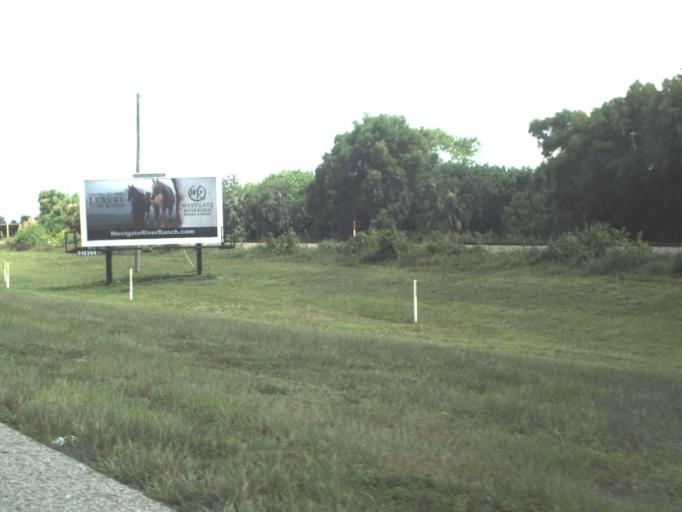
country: US
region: Florida
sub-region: Palm Beach County
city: Mangonia Park
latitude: 26.7822
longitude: -80.1111
